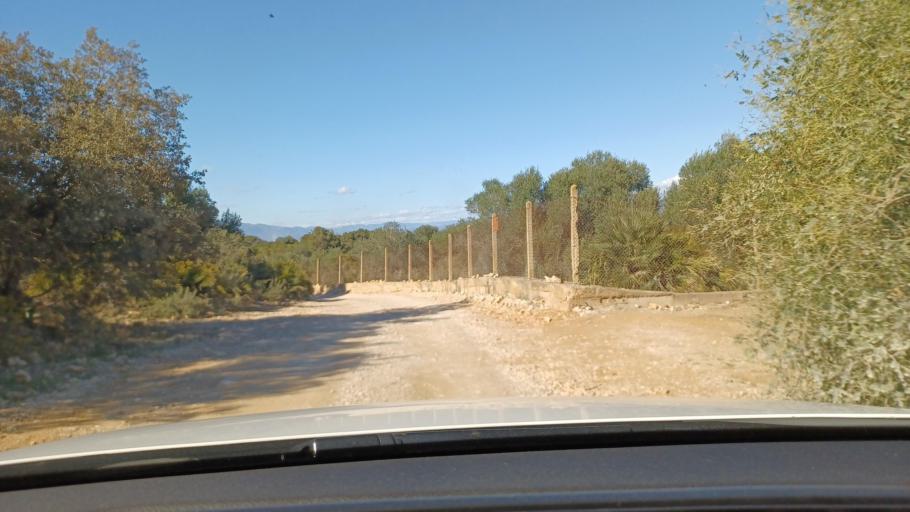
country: ES
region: Catalonia
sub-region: Provincia de Tarragona
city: Masdenverge
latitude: 40.6850
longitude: 0.5375
